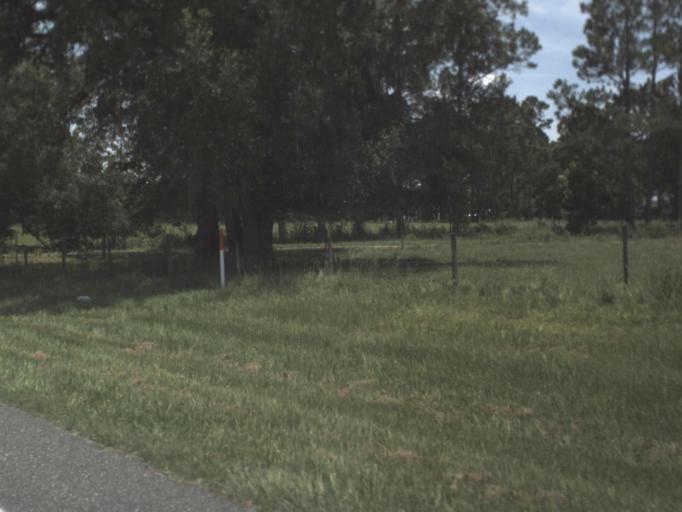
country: US
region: Florida
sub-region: Suwannee County
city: Live Oak
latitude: 30.2105
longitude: -83.0897
